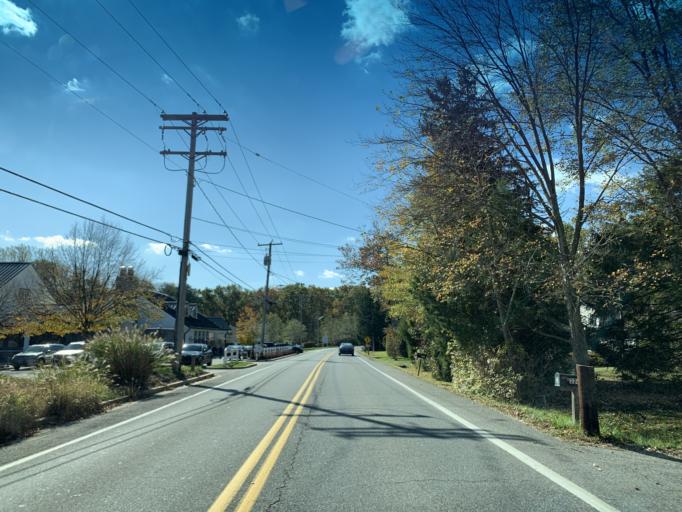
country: US
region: Maryland
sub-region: Anne Arundel County
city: Gambrills
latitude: 39.0731
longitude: -76.6629
